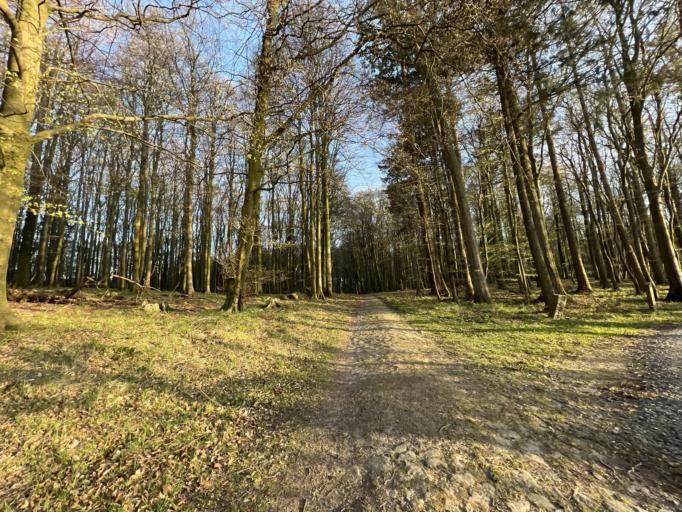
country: DE
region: Mecklenburg-Vorpommern
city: Sassnitz
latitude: 54.5329
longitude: 13.6527
